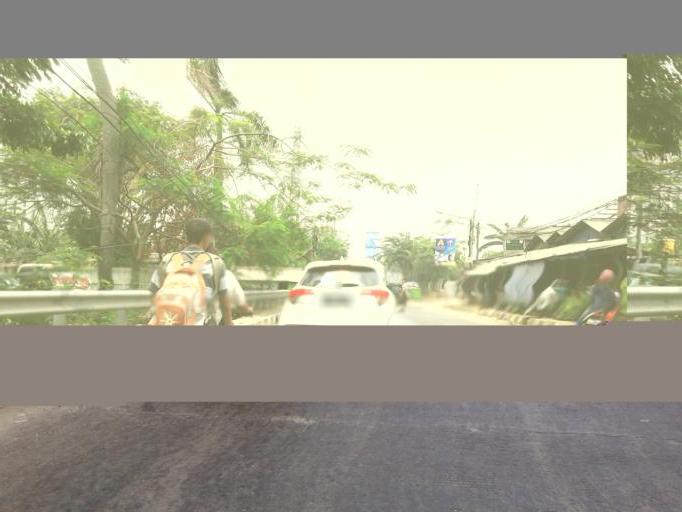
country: ID
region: West Java
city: Pamulang
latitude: -6.3240
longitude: 106.7452
